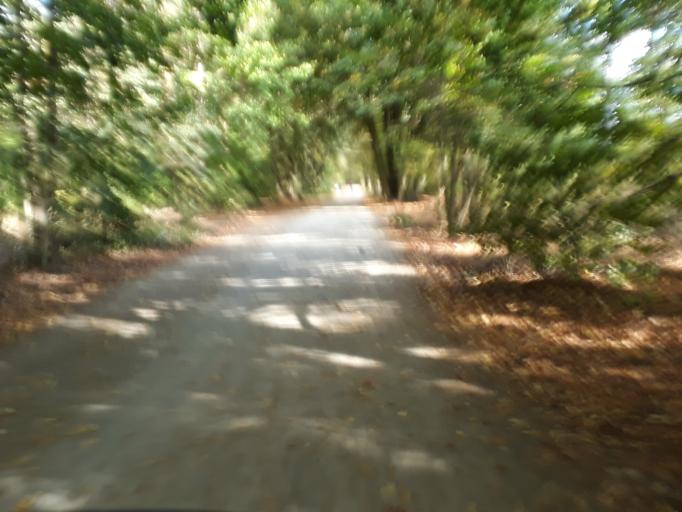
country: DE
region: Berlin
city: Grunewald
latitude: 52.4901
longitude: 13.2382
